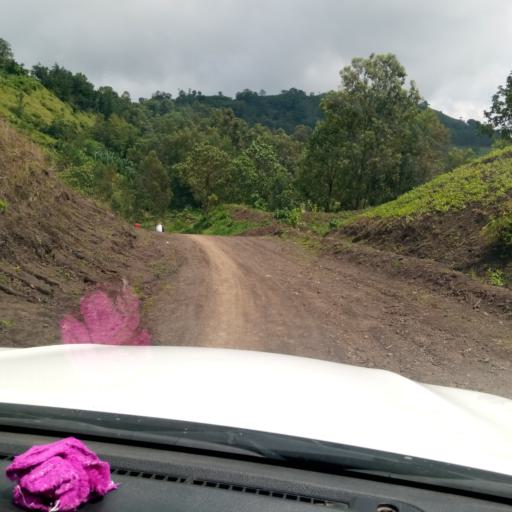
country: ET
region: Southern Nations, Nationalities, and People's Region
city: Arba Minch'
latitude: 6.3133
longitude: 37.3689
